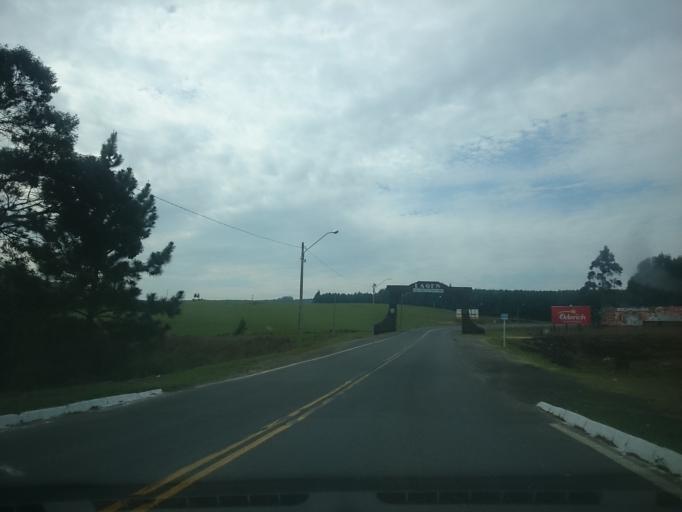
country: BR
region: Santa Catarina
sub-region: Lages
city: Lages
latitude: -27.7506
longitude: -50.3347
